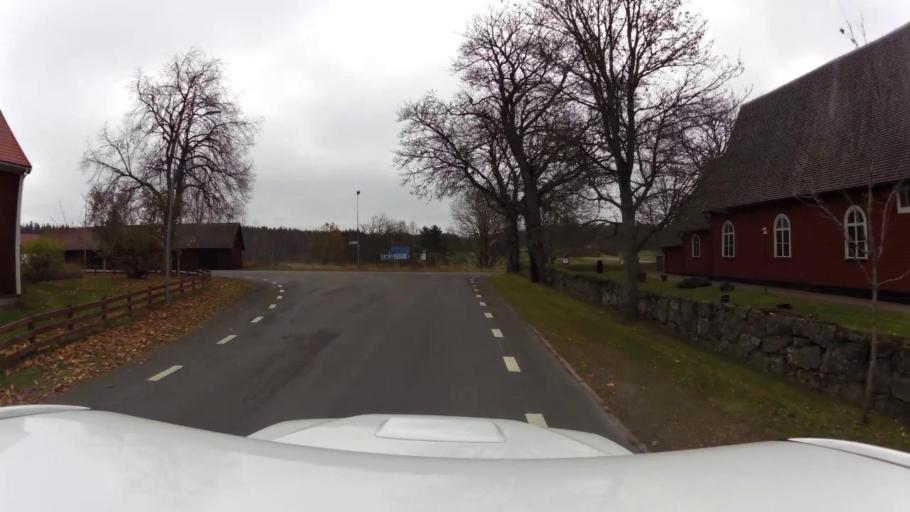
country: SE
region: OEstergoetland
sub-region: Kinda Kommun
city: Kisa
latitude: 58.1241
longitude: 15.4357
